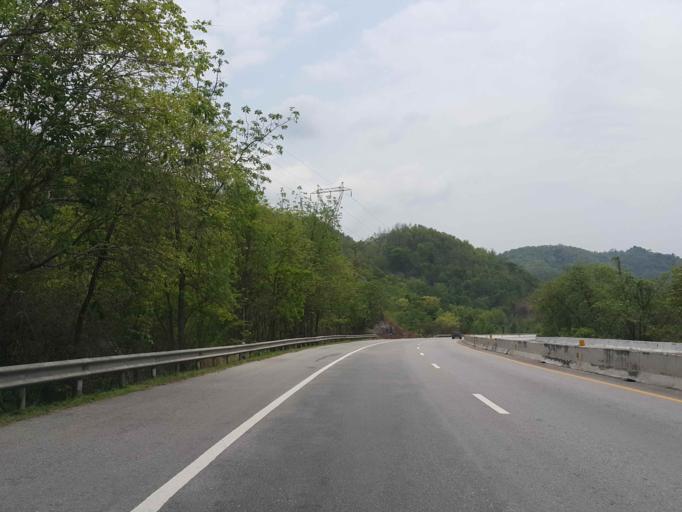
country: TH
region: Lampang
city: Sop Prap
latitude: 17.8414
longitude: 99.2937
